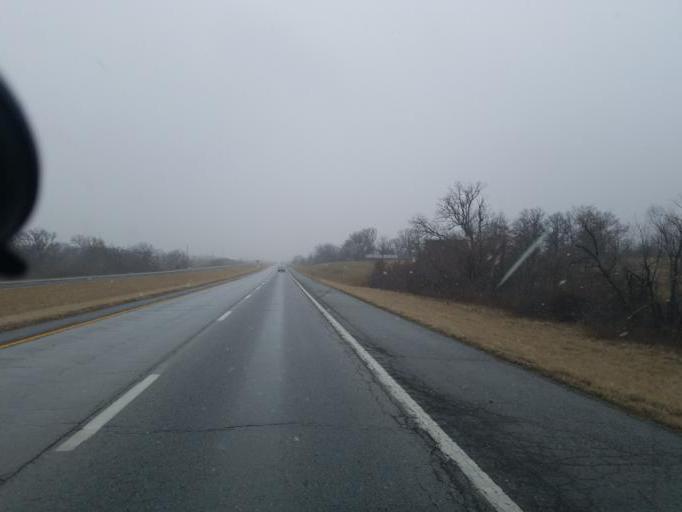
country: US
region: Missouri
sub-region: Macon County
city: La Plata
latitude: 39.9728
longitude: -92.4762
